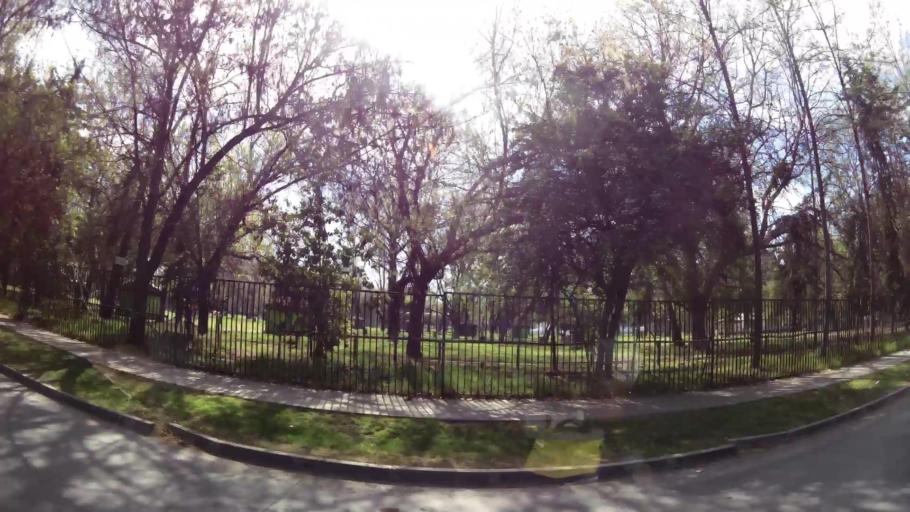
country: CL
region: Santiago Metropolitan
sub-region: Provincia de Santiago
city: Villa Presidente Frei, Nunoa, Santiago, Chile
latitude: -33.4325
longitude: -70.5512
